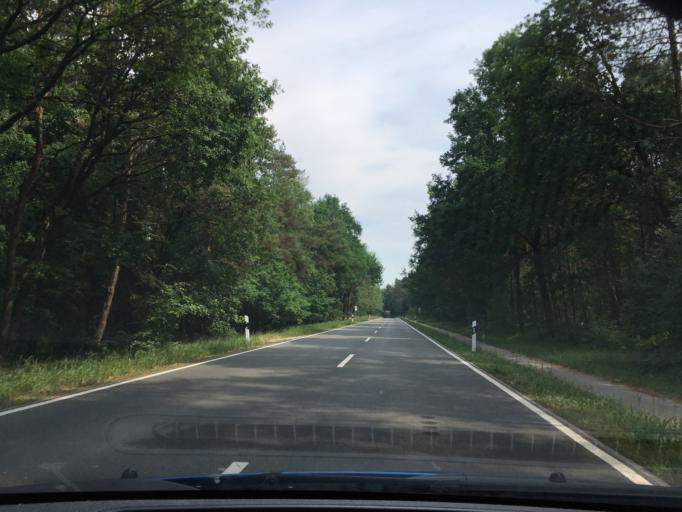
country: DE
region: Lower Saxony
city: Asendorf
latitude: 53.2687
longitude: 9.9580
